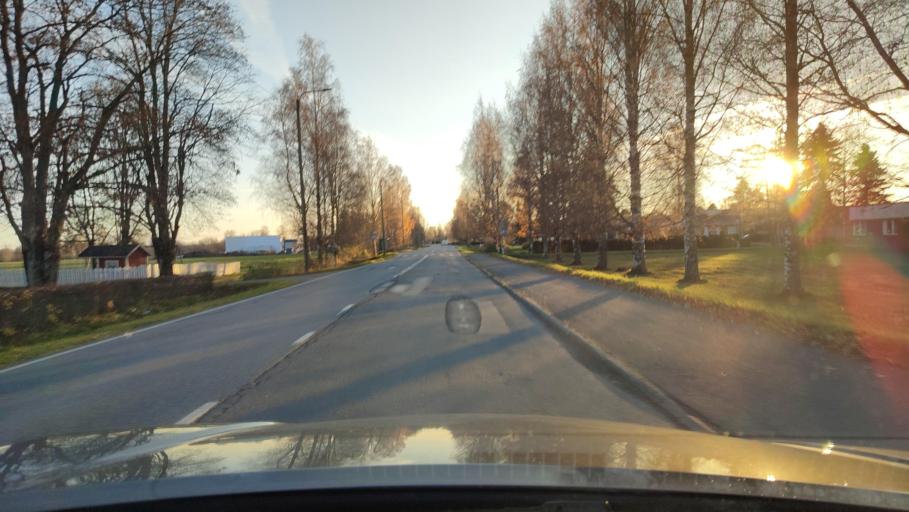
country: FI
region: Ostrobothnia
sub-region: Sydosterbotten
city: Naerpes
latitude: 62.6060
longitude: 21.4606
